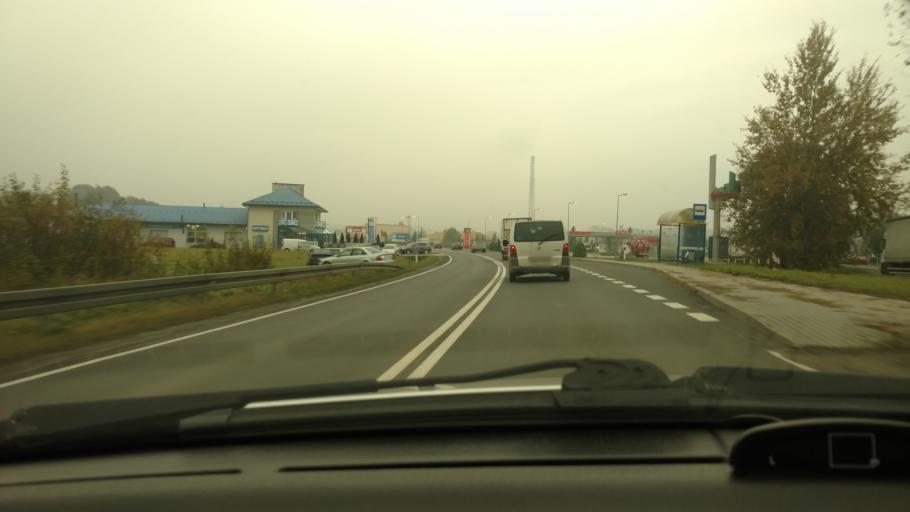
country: PL
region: Lesser Poland Voivodeship
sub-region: Powiat gorlicki
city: Kobylanka
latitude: 49.6861
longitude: 21.1914
